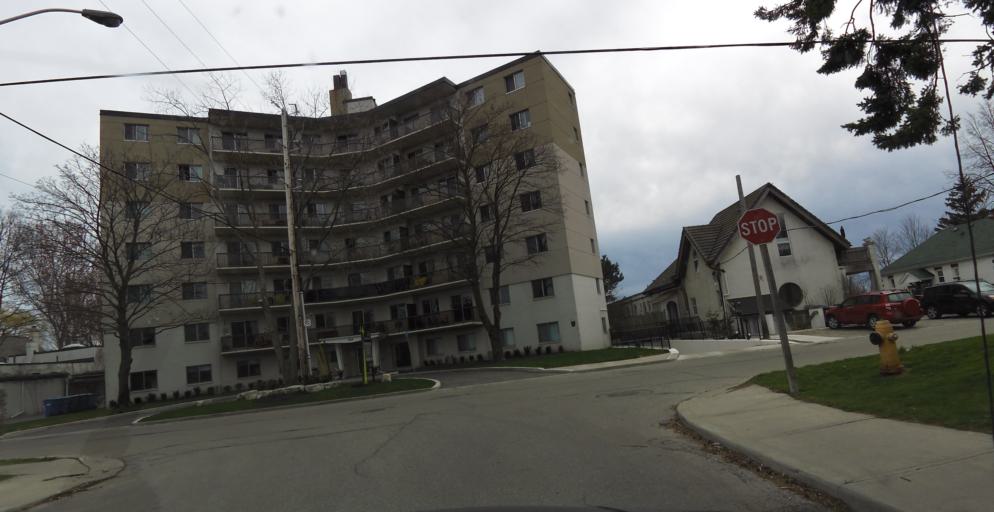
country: CA
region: Ontario
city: Etobicoke
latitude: 43.5945
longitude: -79.5099
